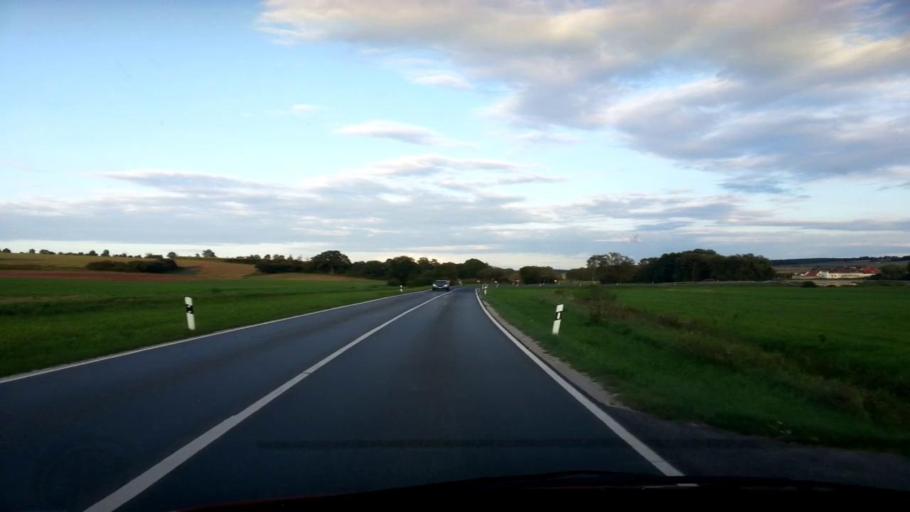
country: DE
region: Bavaria
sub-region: Upper Franconia
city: Burgebrach
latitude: 49.8215
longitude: 10.6741
